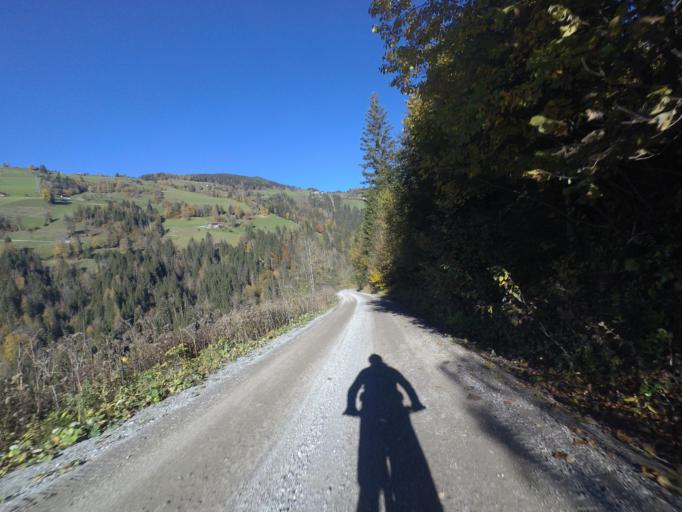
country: AT
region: Salzburg
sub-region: Politischer Bezirk Sankt Johann im Pongau
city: Sankt Johann im Pongau
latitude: 47.3298
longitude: 13.2393
